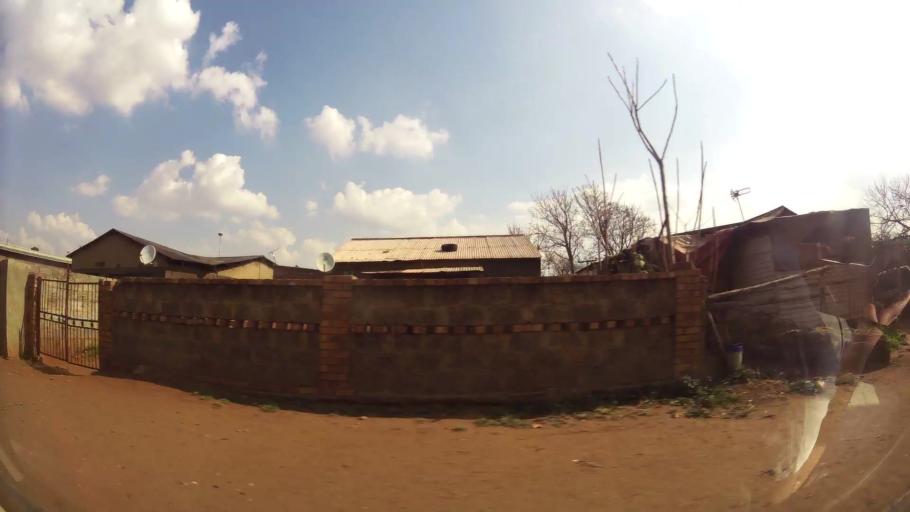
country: ZA
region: Gauteng
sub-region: Ekurhuleni Metropolitan Municipality
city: Germiston
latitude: -26.3089
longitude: 28.1601
